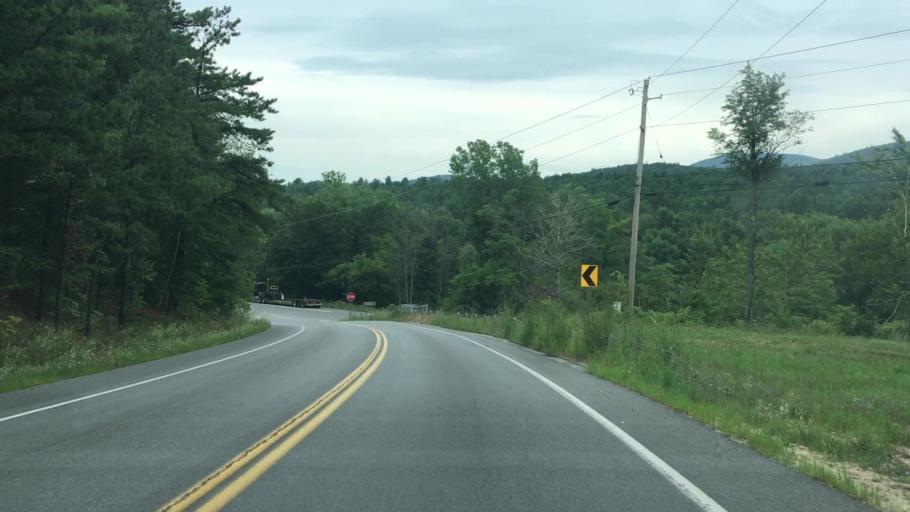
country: US
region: New York
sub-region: Essex County
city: Keeseville
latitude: 44.4656
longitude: -73.5886
